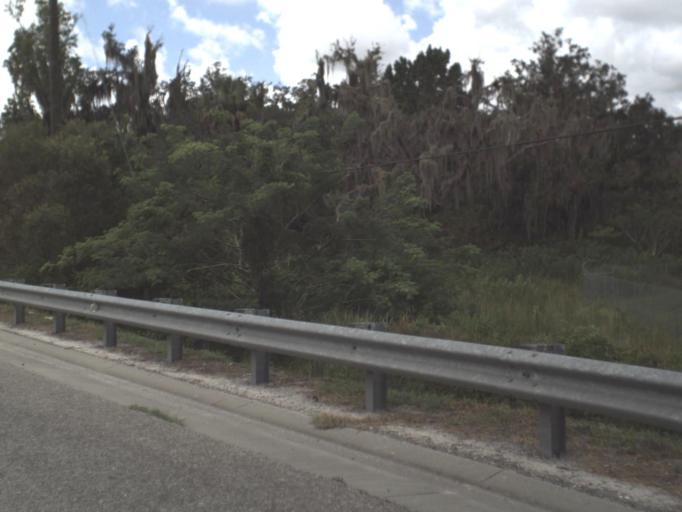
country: US
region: Florida
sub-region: Hardee County
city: Wauchula
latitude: 27.5256
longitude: -81.8093
